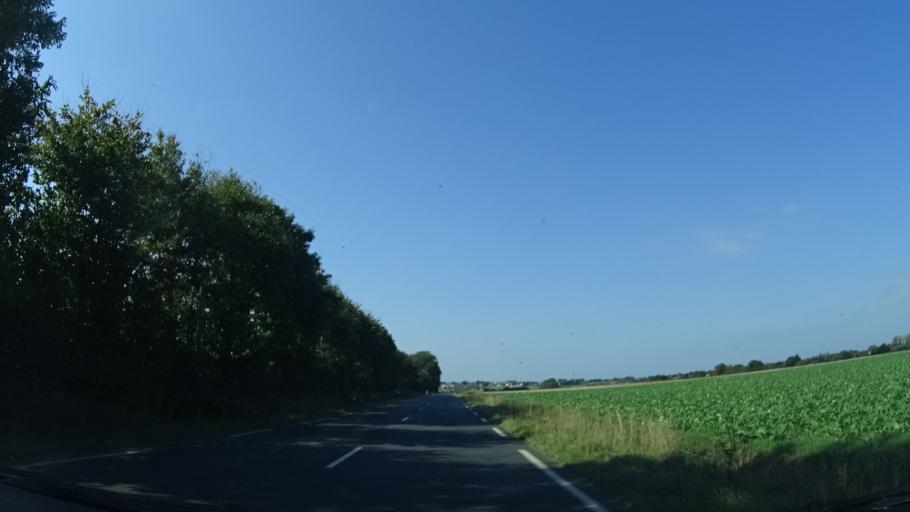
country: FR
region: Brittany
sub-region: Departement du Finistere
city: Plonevez-Porzay
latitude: 48.1317
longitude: -4.1945
